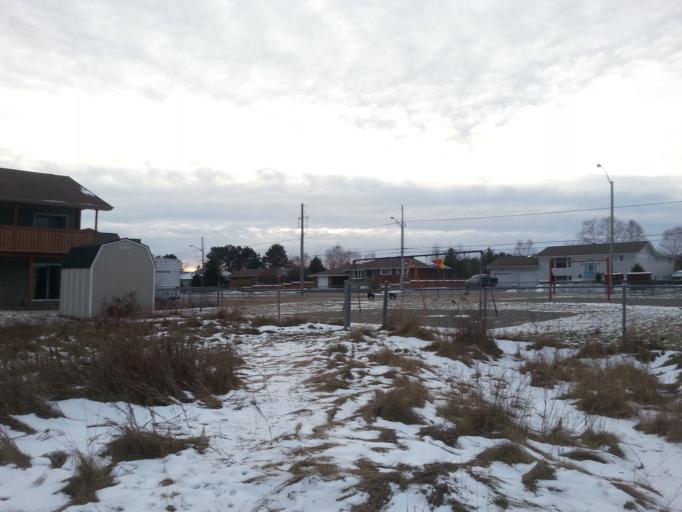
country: CA
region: Ontario
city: Greater Sudbury
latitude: 46.6166
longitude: -81.0352
